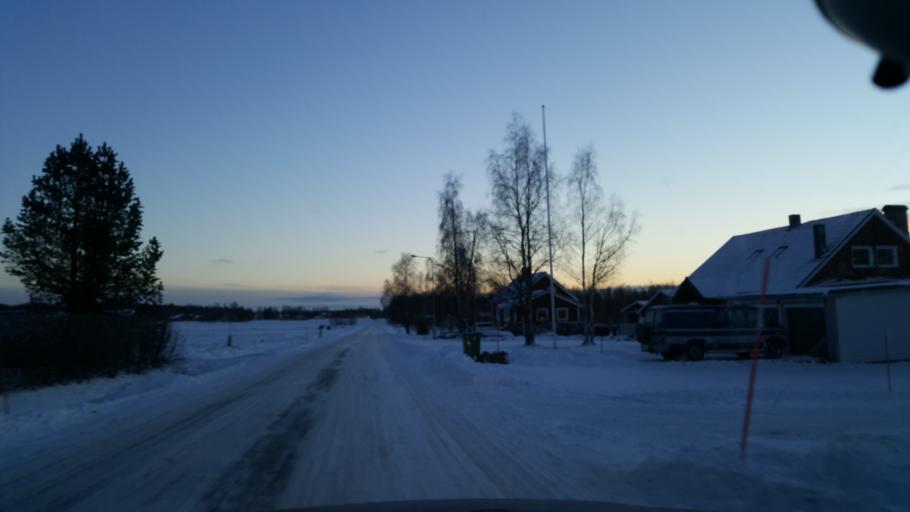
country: SE
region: Norrbotten
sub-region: Lulea Kommun
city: Sodra Sunderbyn
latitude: 65.5405
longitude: 21.9022
